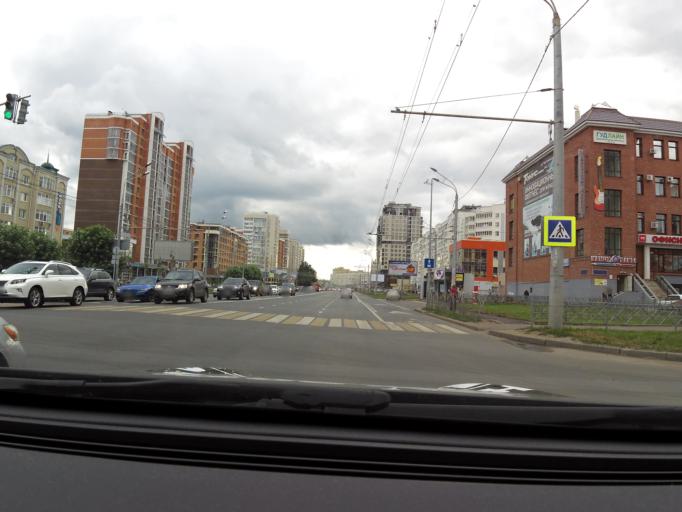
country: RU
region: Tatarstan
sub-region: Gorod Kazan'
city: Kazan
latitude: 55.8194
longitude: 49.1158
